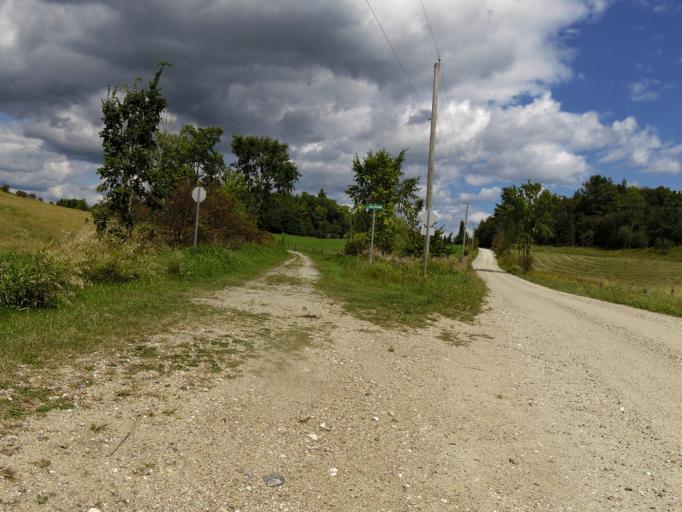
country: CA
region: Quebec
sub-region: Outaouais
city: Wakefield
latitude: 45.8334
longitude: -75.9783
